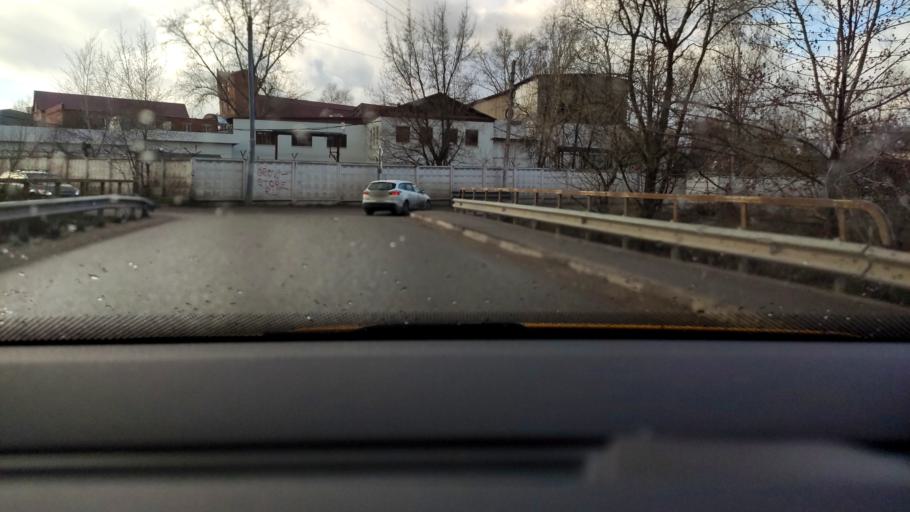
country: RU
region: Moskovskaya
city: Saltykovka
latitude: 55.7435
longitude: 37.9592
